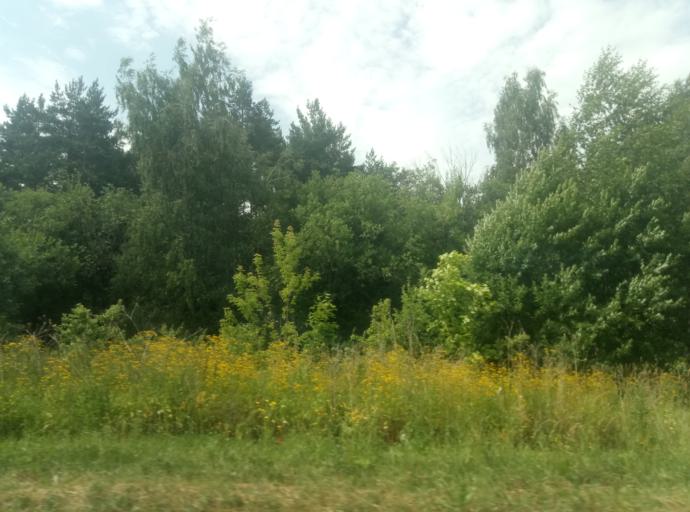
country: RU
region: Tula
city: Bogoroditsk
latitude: 53.8317
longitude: 38.1096
